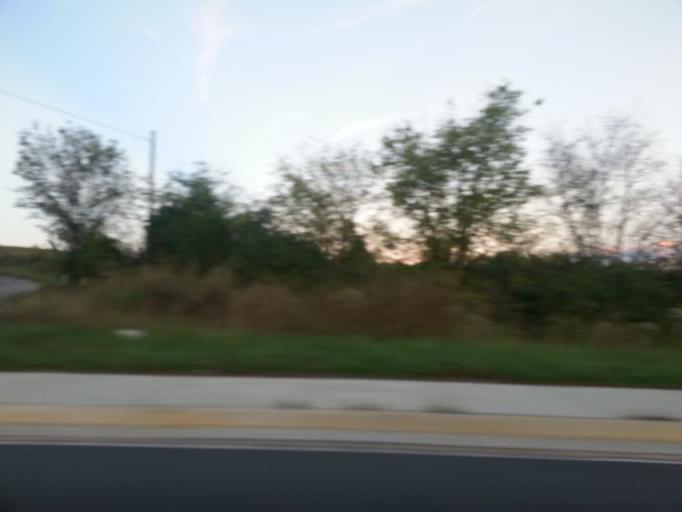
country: US
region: Tennessee
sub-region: Sevier County
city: Sevierville
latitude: 35.9316
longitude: -83.5828
